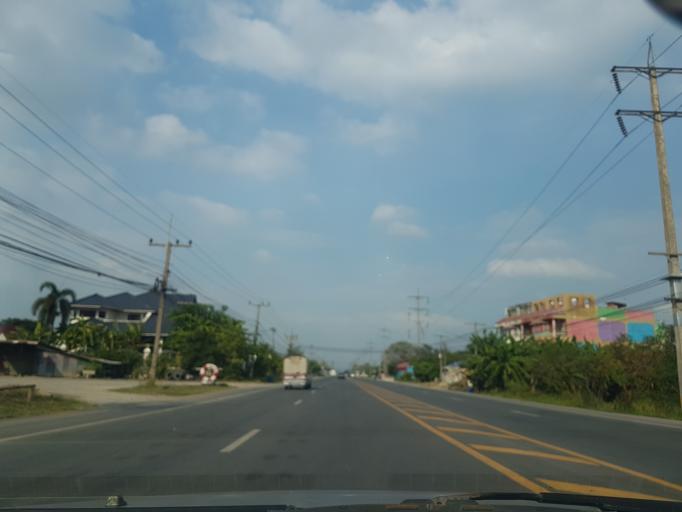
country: TH
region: Phra Nakhon Si Ayutthaya
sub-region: Amphoe Tha Ruea
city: Tha Ruea
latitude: 14.5806
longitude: 100.7290
